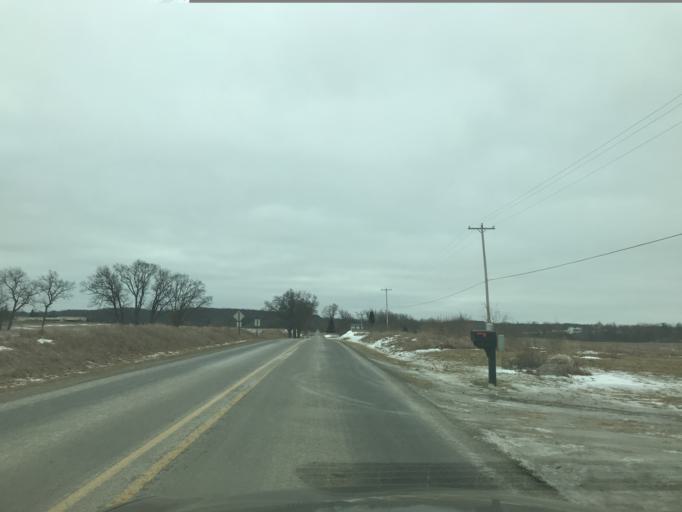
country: US
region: Michigan
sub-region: Lenawee County
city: Manitou Beach-Devils Lake
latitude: 42.0564
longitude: -84.3258
